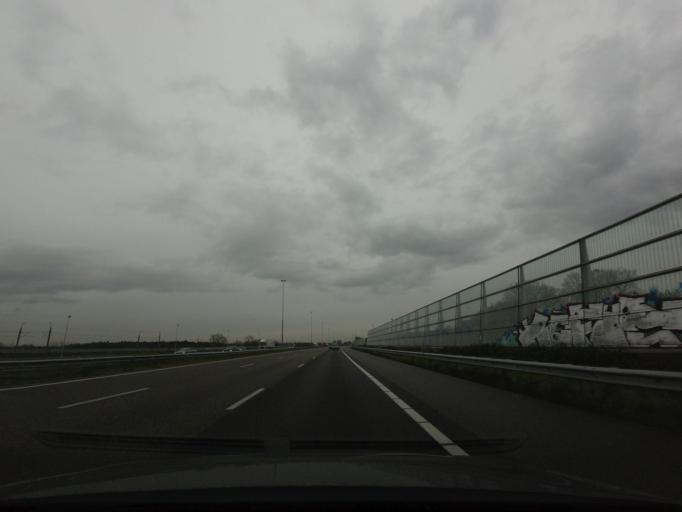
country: NL
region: North Brabant
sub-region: Gemeente Breda
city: Breda
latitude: 51.5617
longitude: 4.7337
